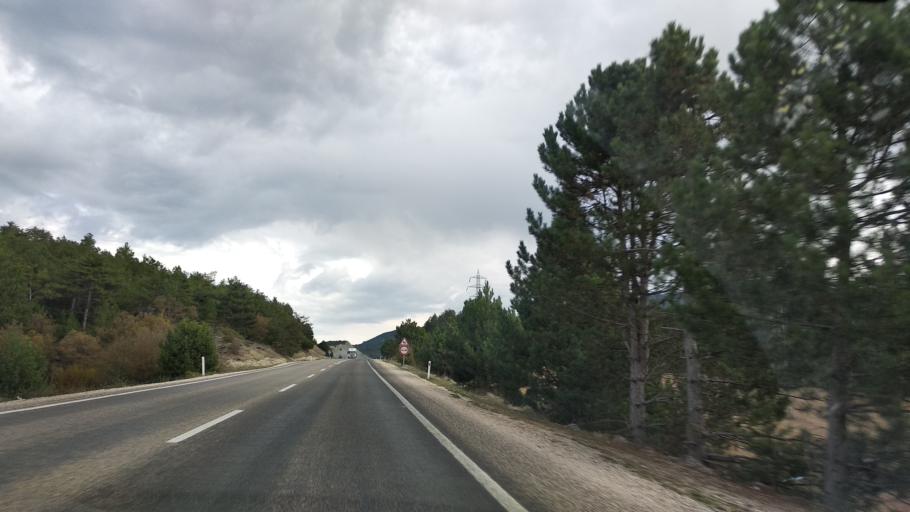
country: TR
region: Bolu
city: Mudurnu
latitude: 40.4857
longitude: 31.1888
